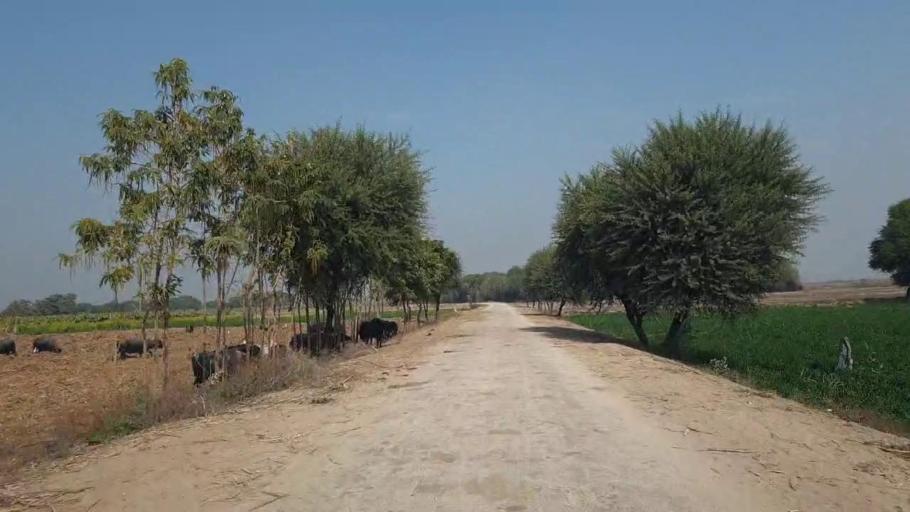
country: PK
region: Sindh
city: Chambar
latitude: 25.3449
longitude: 68.8517
